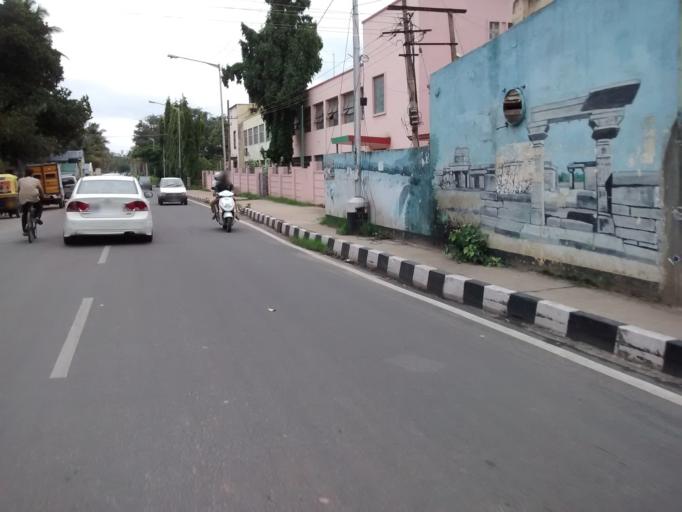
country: IN
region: Karnataka
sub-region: Bangalore Urban
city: Yelahanka
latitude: 13.0413
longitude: 77.5893
